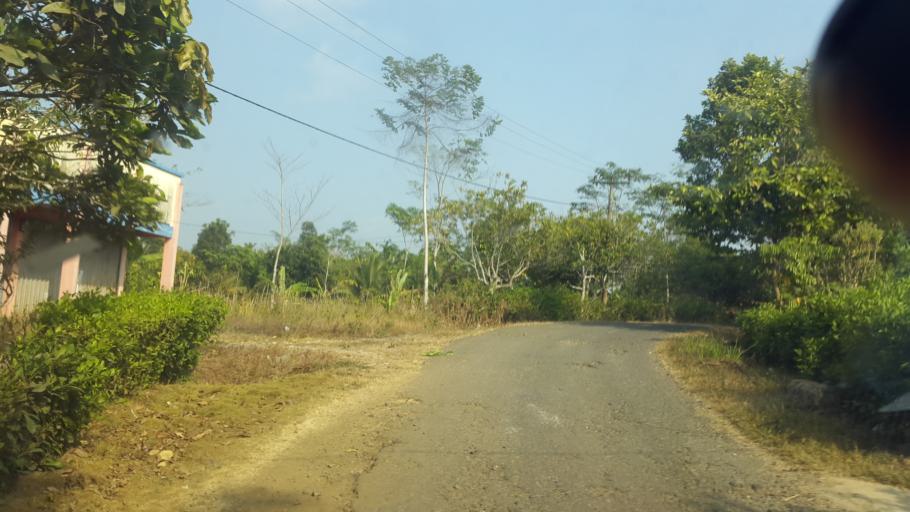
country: ID
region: West Java
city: Pasirmalang
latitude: -7.2494
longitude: 106.6141
